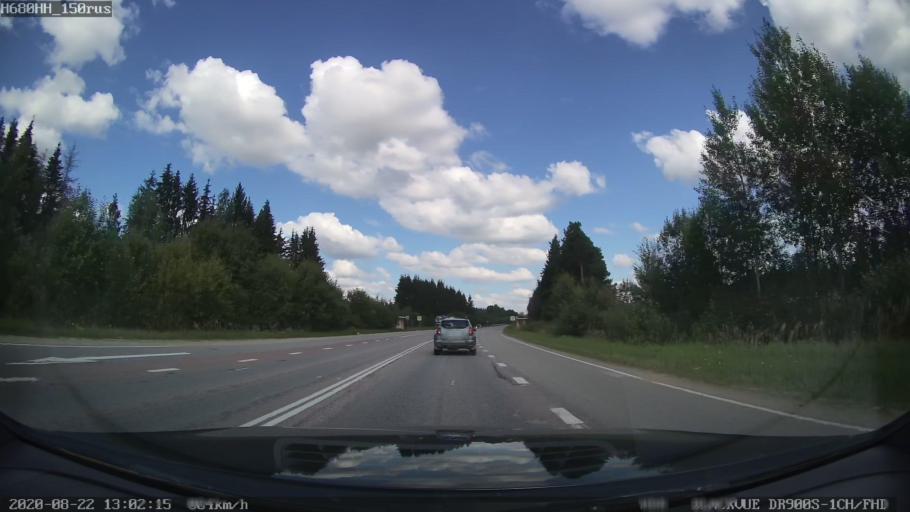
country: RU
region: Tverskaya
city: Bezhetsk
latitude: 57.6466
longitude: 36.3952
